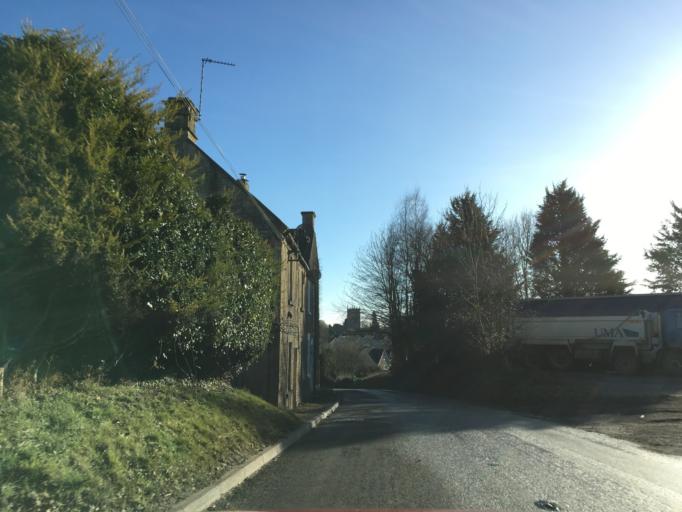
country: GB
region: England
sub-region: Wiltshire
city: Nettleton
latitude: 51.5155
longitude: -2.2713
